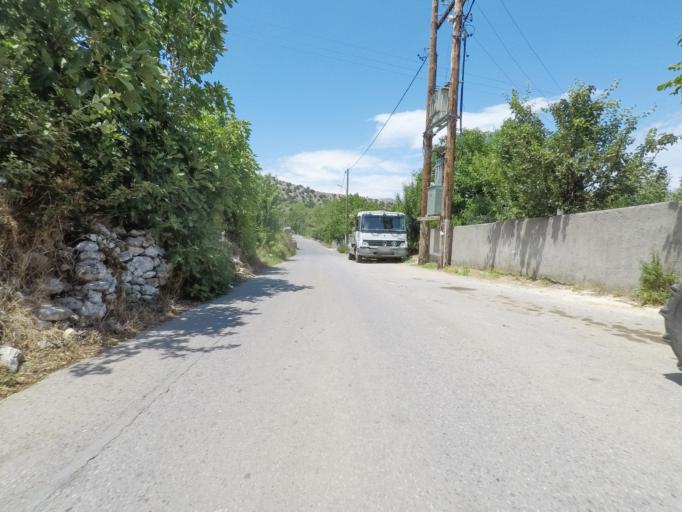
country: GR
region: Crete
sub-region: Nomos Irakleiou
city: Mokhos
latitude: 35.1699
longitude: 25.4381
